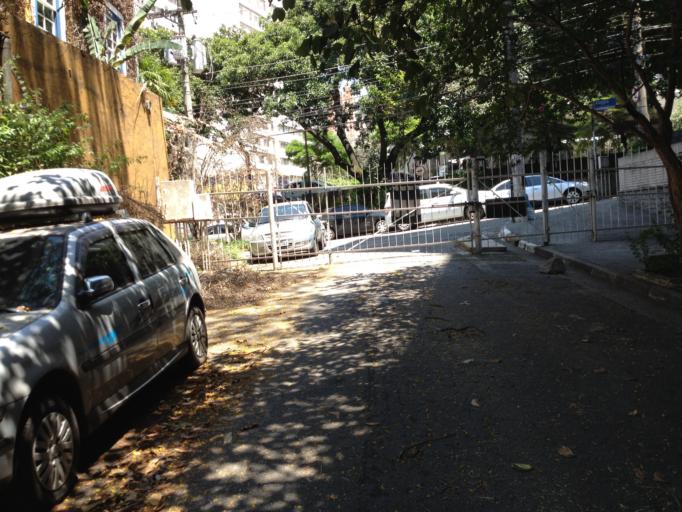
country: BR
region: Sao Paulo
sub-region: Sao Paulo
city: Sao Paulo
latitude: -23.5620
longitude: -46.6734
